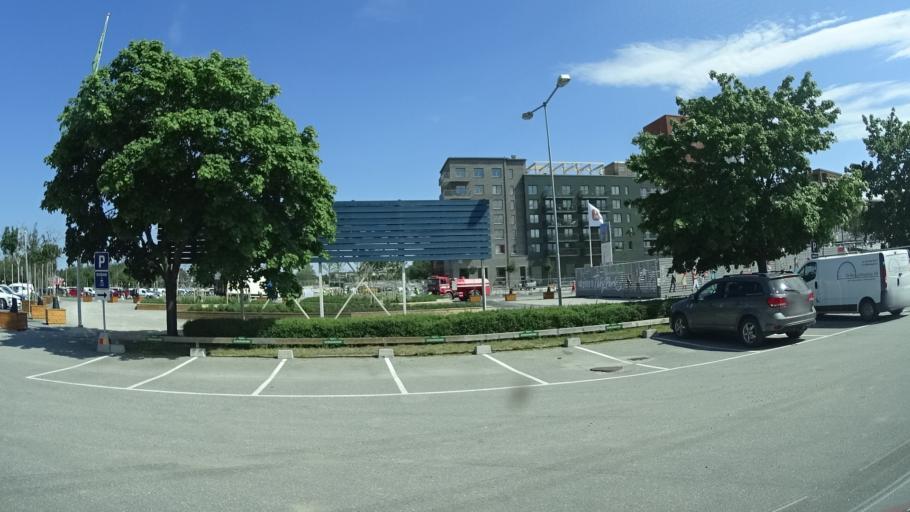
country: SE
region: Stockholm
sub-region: Taby Kommun
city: Taby
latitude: 59.4448
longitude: 18.0848
